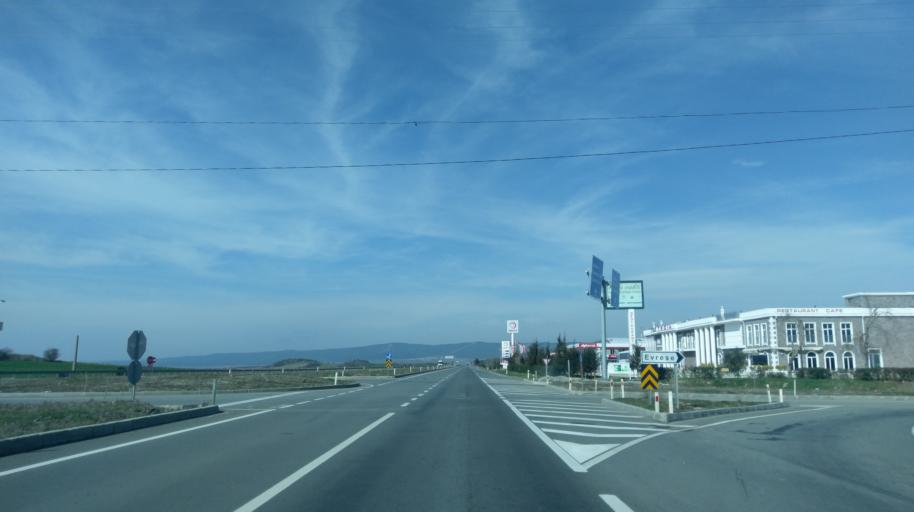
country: TR
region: Canakkale
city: Evrese
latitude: 40.6391
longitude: 26.8601
